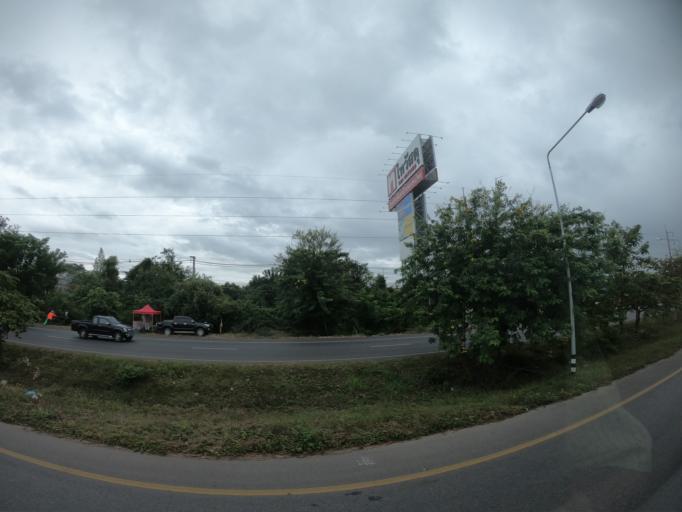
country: TH
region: Roi Et
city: Roi Et
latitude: 16.0569
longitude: 103.6197
